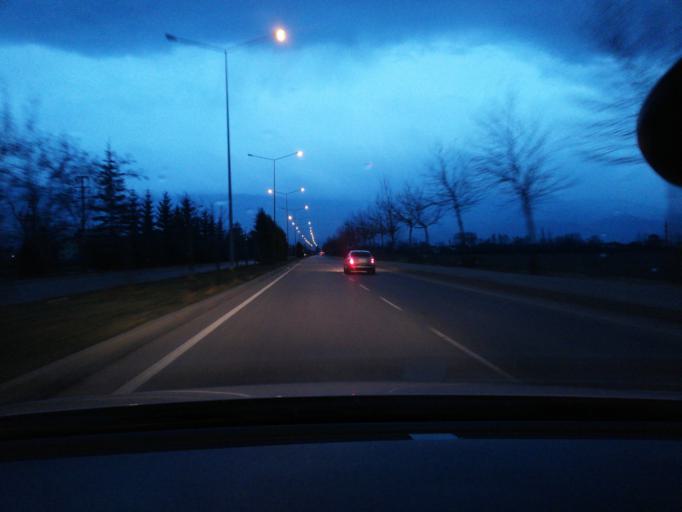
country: TR
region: Bolu
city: Bolu
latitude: 40.7204
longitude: 31.6134
